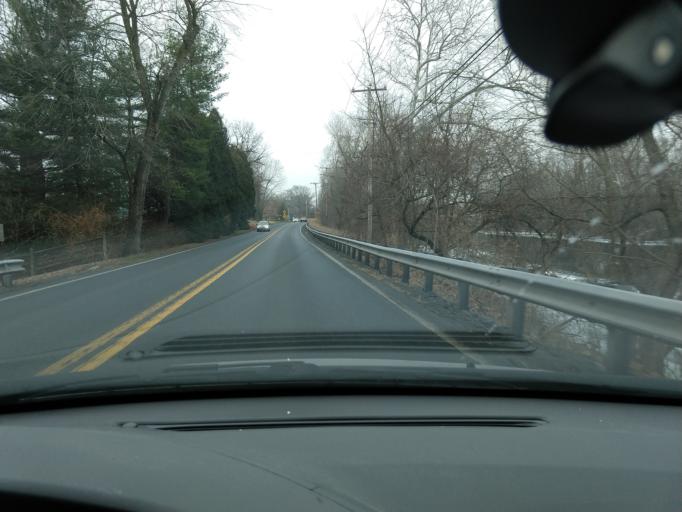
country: US
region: Pennsylvania
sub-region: Berks County
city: Amity Gardens
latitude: 40.2482
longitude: -75.7210
